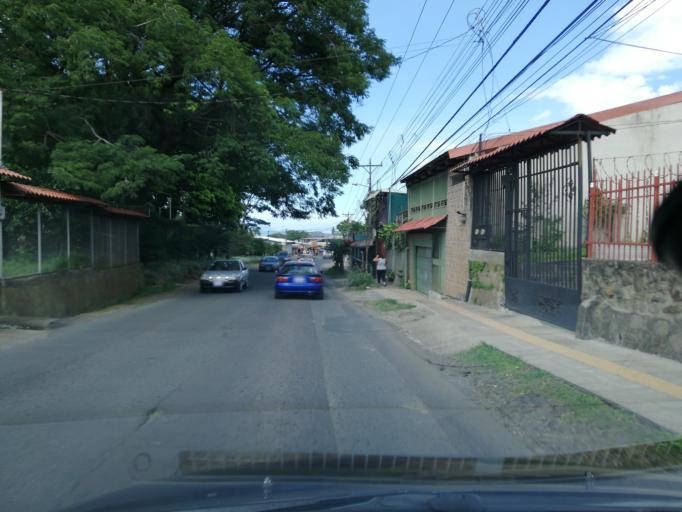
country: CR
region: Alajuela
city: Alajuela
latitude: 9.9923
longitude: -84.2351
